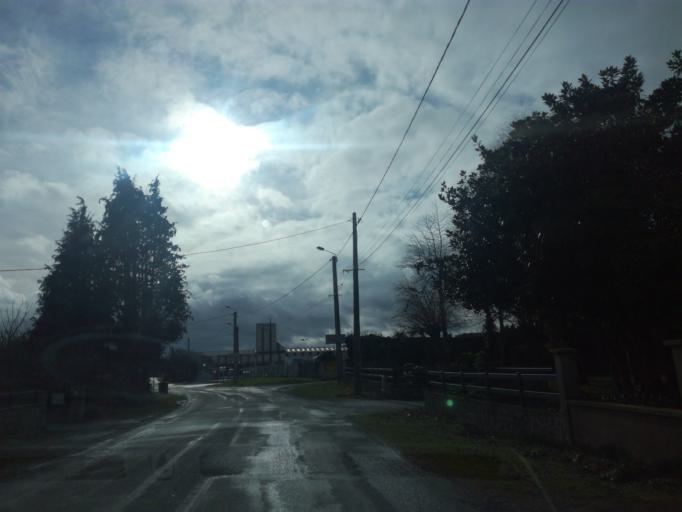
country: FR
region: Brittany
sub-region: Departement du Morbihan
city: Le Sourn
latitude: 48.0379
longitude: -2.9717
